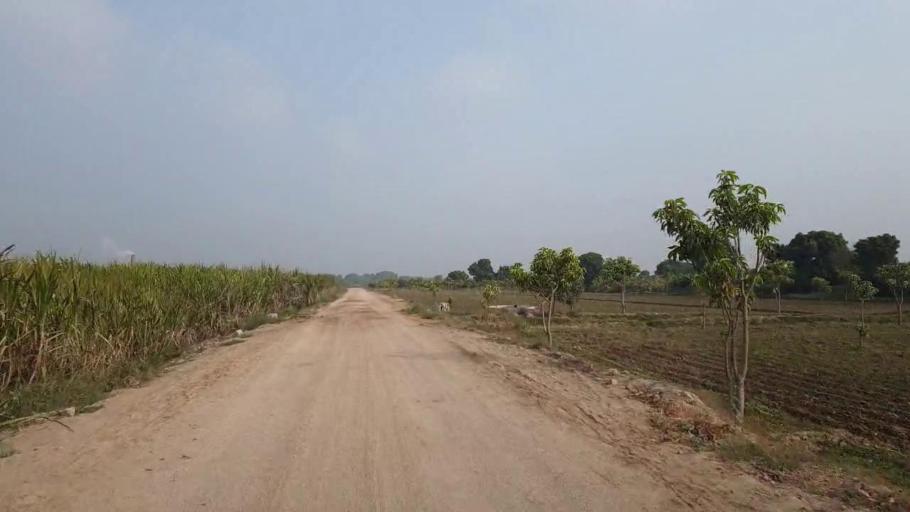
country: PK
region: Sindh
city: Tando Muhammad Khan
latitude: 25.1633
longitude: 68.5934
